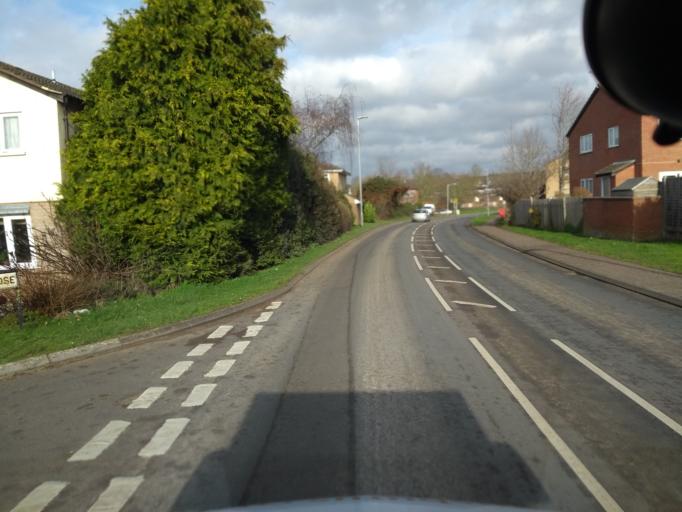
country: GB
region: England
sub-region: Somerset
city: Taunton
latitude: 51.0028
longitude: -3.0823
